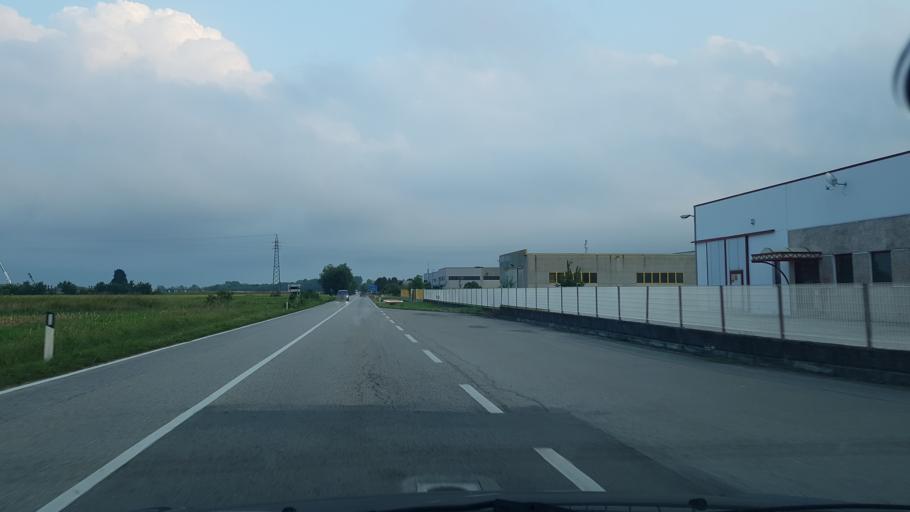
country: IT
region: Friuli Venezia Giulia
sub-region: Provincia di Udine
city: Ialmicco
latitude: 45.9253
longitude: 13.3699
